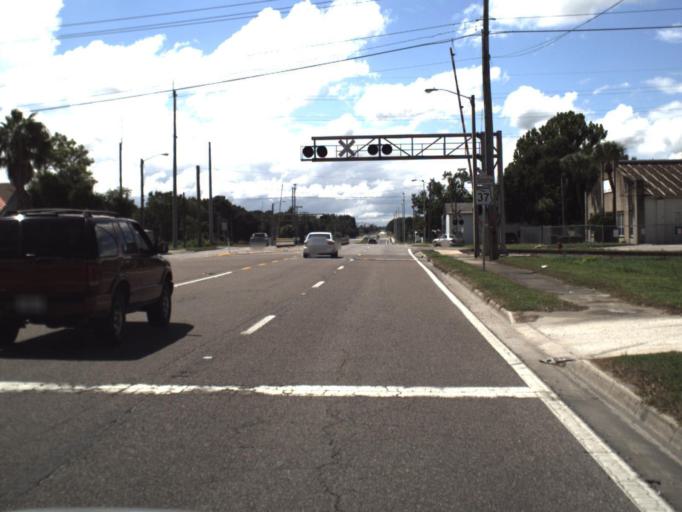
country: US
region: Florida
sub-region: Polk County
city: Mulberry
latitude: 27.8945
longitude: -81.9737
